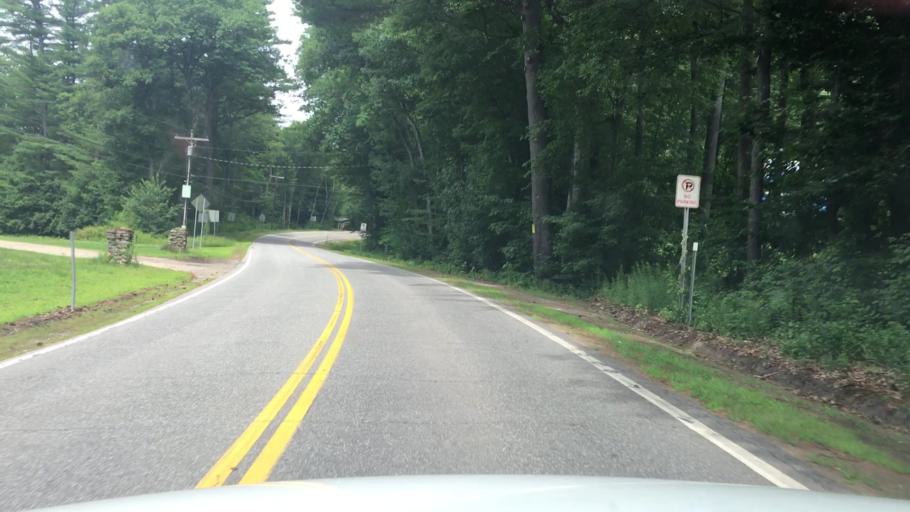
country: US
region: New Hampshire
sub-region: Grafton County
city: Plymouth
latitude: 43.7622
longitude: -71.6724
